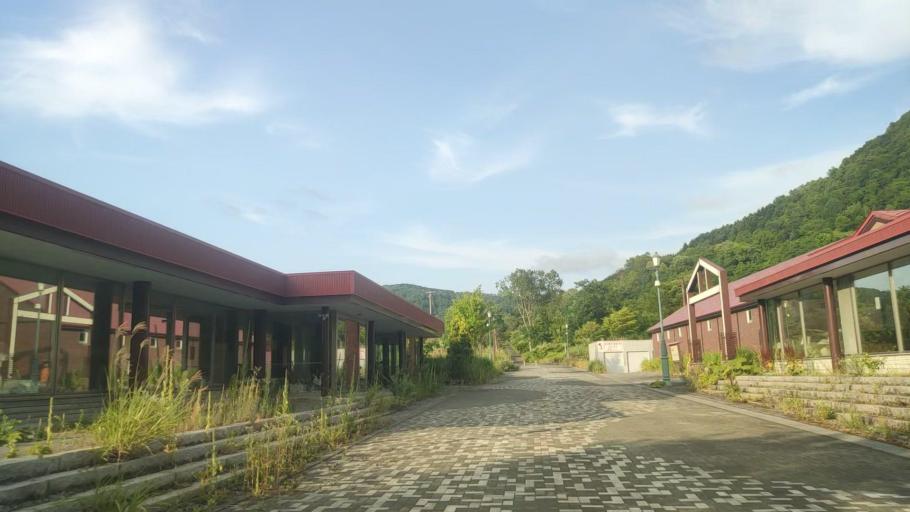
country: JP
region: Hokkaido
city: Iwamizawa
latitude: 43.0644
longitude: 141.9867
